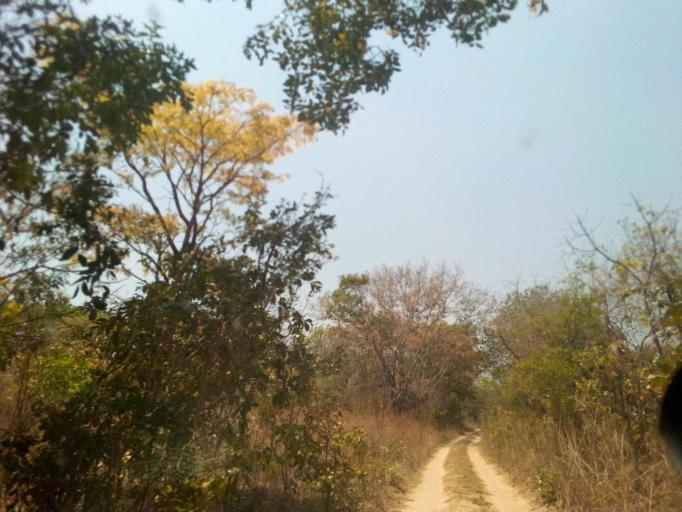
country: ZM
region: Copperbelt
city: Kataba
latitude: -12.2535
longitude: 30.3879
